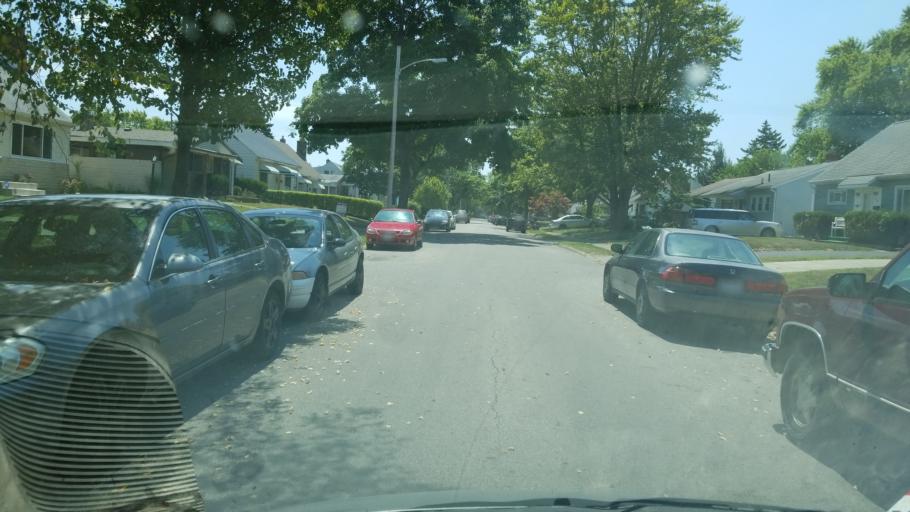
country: US
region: Ohio
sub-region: Franklin County
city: Lincoln Village
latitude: 39.9406
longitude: -83.1060
